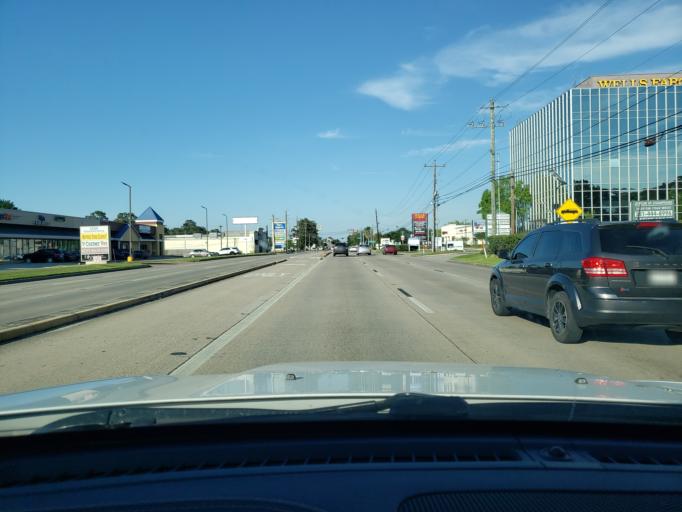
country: US
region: Texas
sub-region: Harris County
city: Hudson
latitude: 29.9784
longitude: -95.5155
